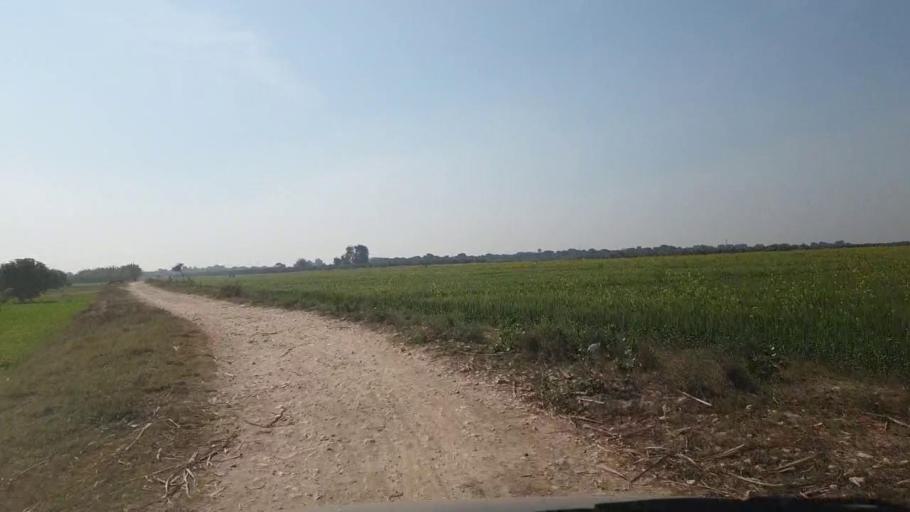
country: PK
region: Sindh
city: Tando Allahyar
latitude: 25.3967
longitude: 68.7816
